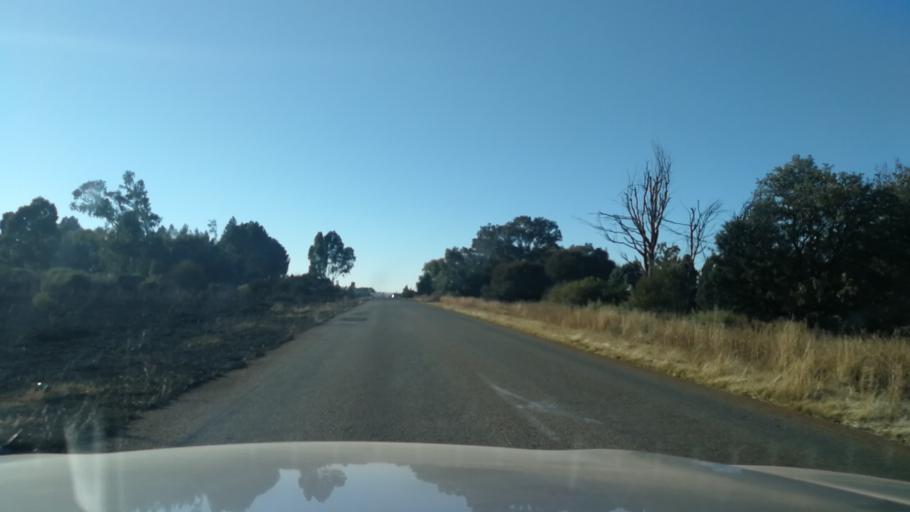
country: ZA
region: North-West
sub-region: Bojanala Platinum District Municipality
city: Rustenburg
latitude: -25.9526
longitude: 27.1839
